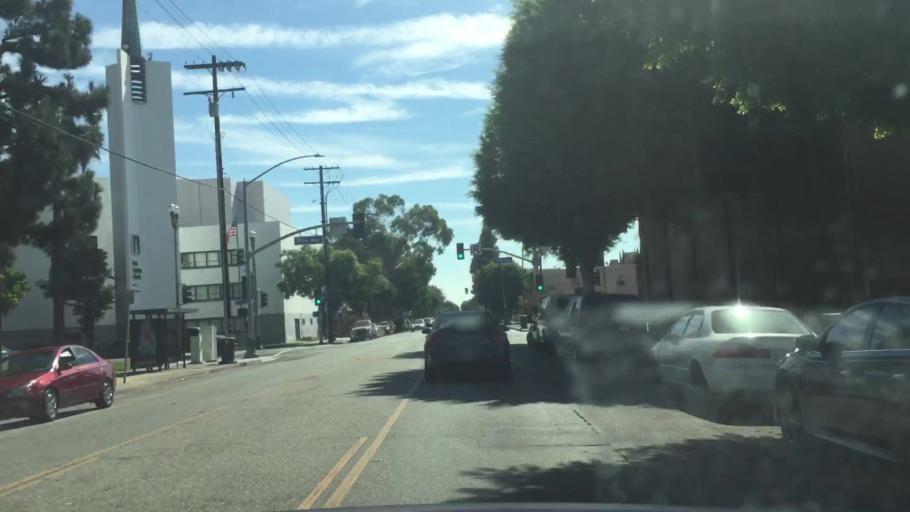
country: US
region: California
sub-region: Los Angeles County
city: Long Beach
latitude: 33.7789
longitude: -118.1930
